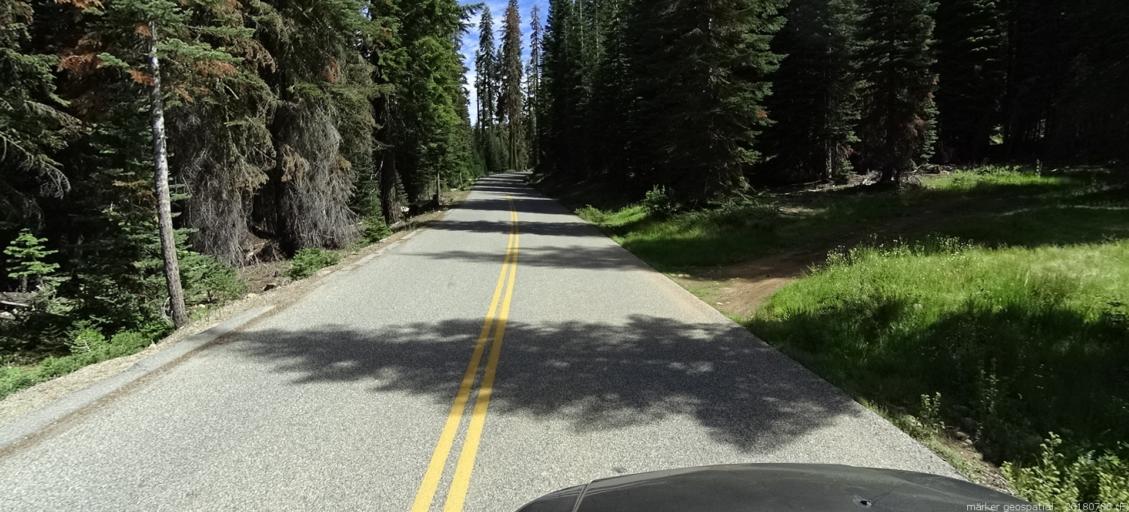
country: US
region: California
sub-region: Madera County
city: Oakhurst
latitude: 37.4084
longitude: -119.4987
